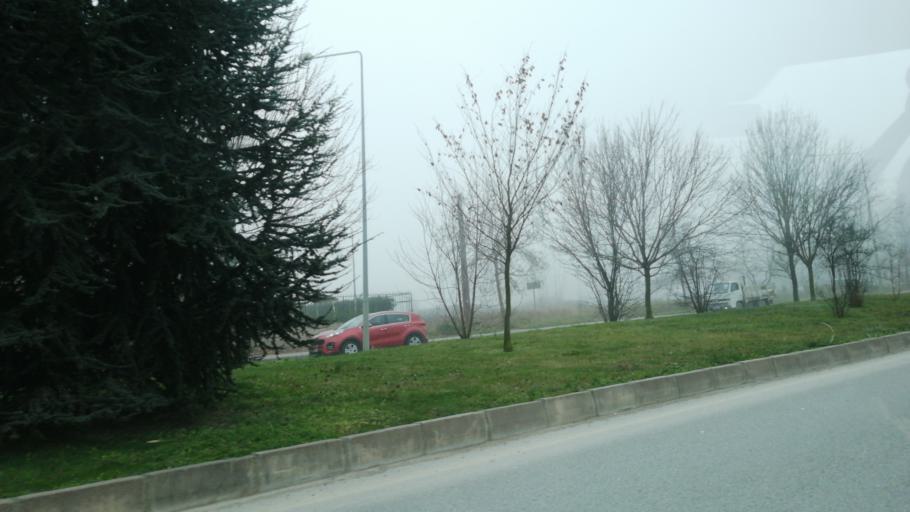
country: TR
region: Yalova
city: Yalova
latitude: 40.6517
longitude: 29.2427
